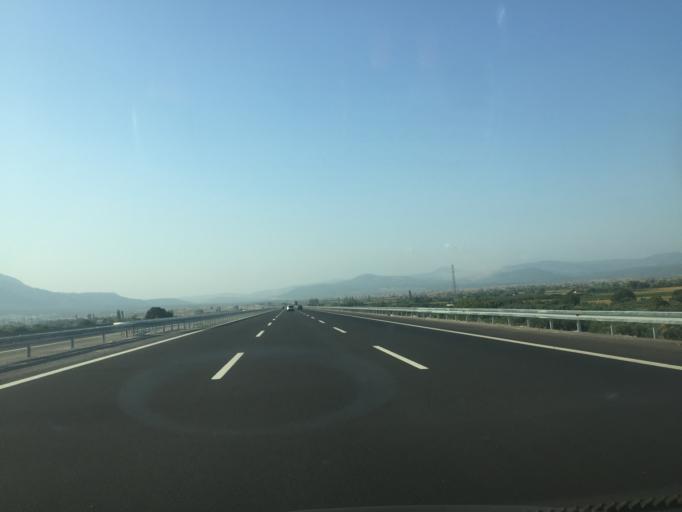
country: TR
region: Manisa
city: Kirkagac
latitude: 39.0739
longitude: 27.7165
